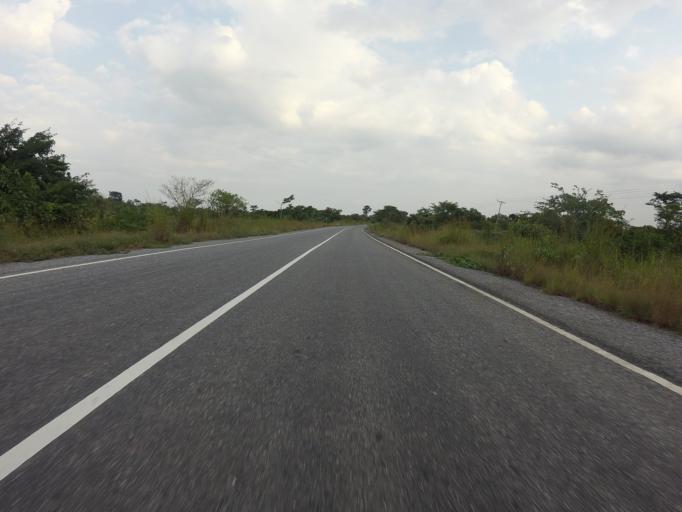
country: GH
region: Volta
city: Ho
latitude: 6.3425
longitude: 0.5392
